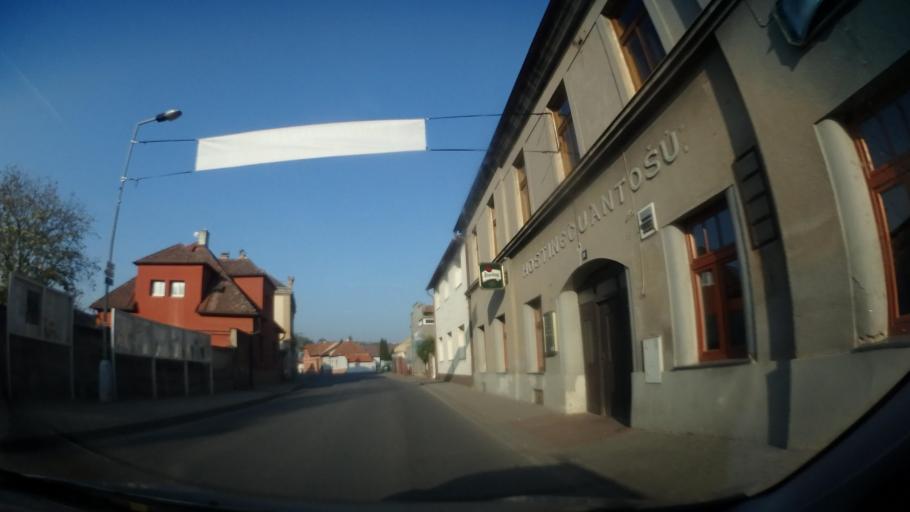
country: CZ
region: Central Bohemia
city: Jirny
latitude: 50.1158
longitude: 14.6984
